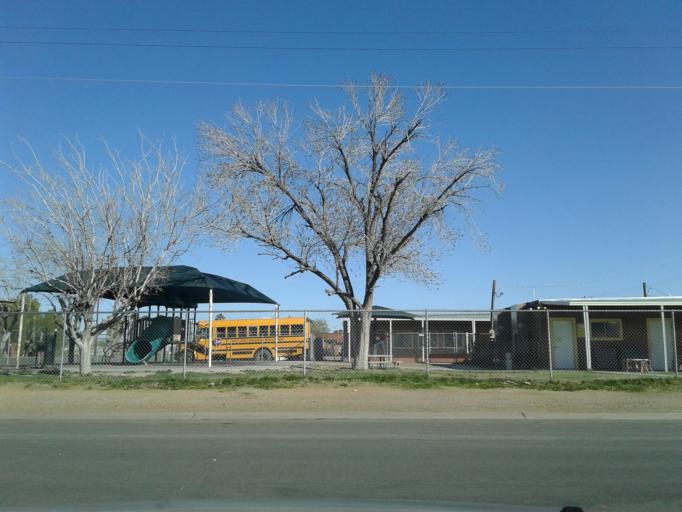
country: US
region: Arizona
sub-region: Pinal County
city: Eloy
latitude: 32.7509
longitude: -111.5501
